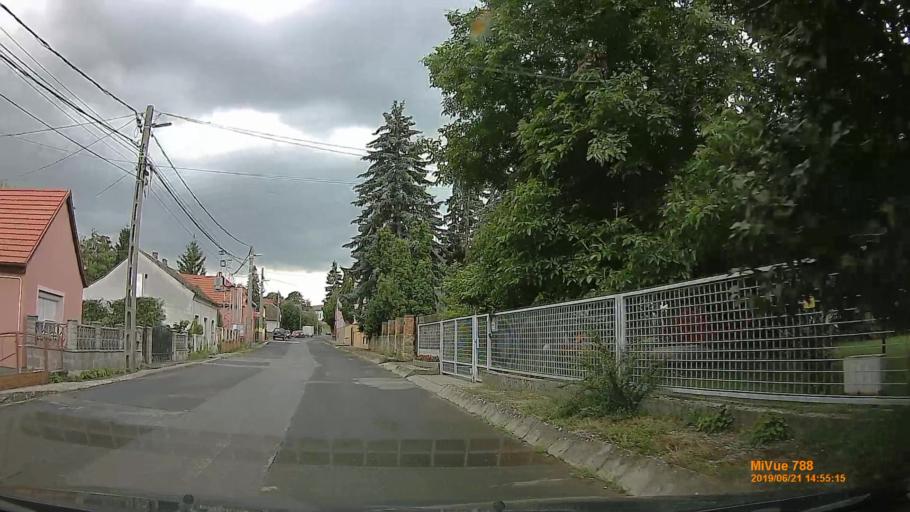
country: HU
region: Baranya
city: Hosszuheteny
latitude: 46.1244
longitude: 18.3112
